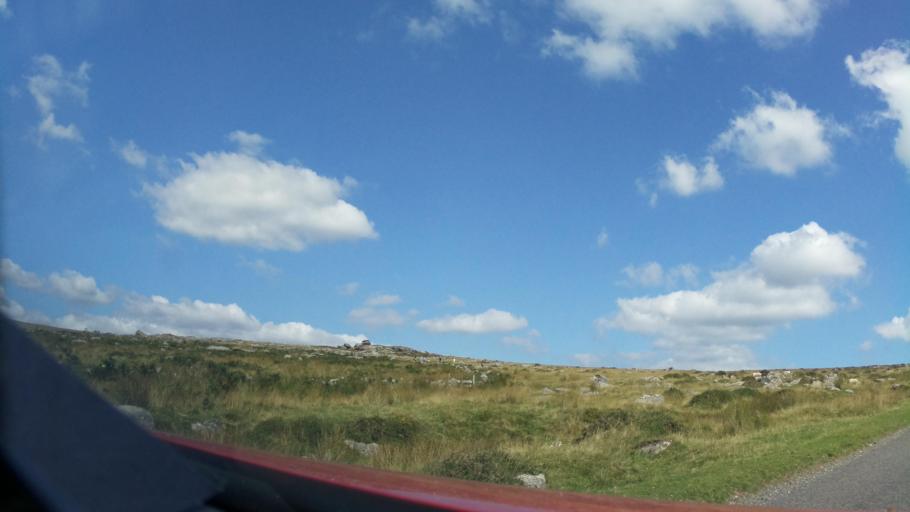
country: GB
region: England
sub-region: Devon
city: Horrabridge
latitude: 50.5578
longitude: -4.0414
